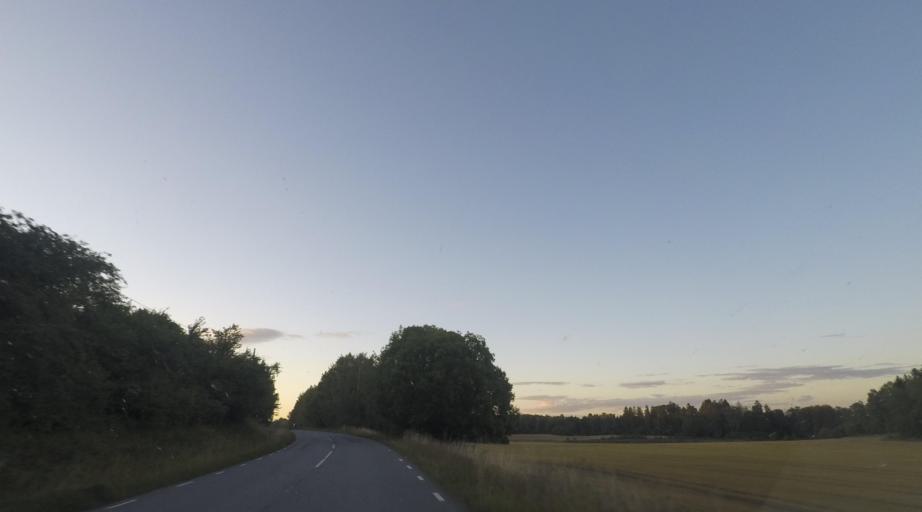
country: SE
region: Soedermanland
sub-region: Trosa Kommun
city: Trosa
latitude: 58.9751
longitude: 17.6931
